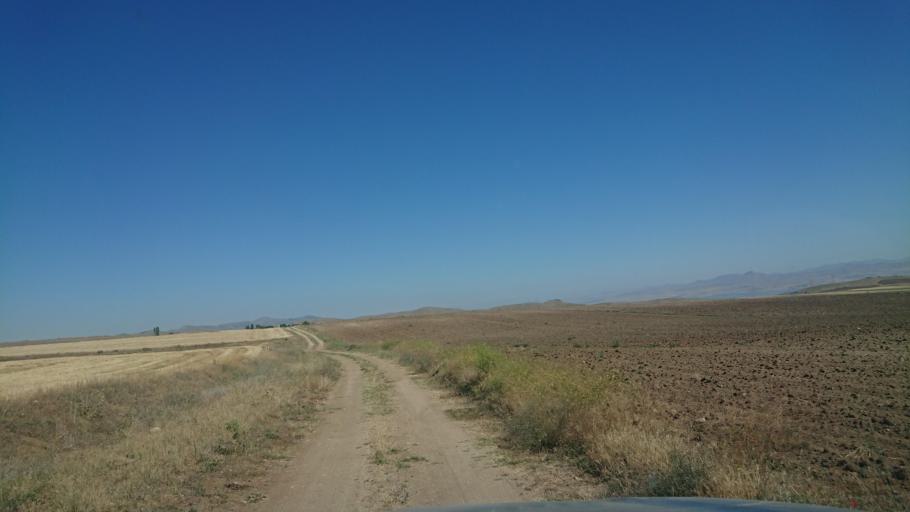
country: TR
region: Aksaray
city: Sariyahsi
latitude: 38.9334
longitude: 33.8446
